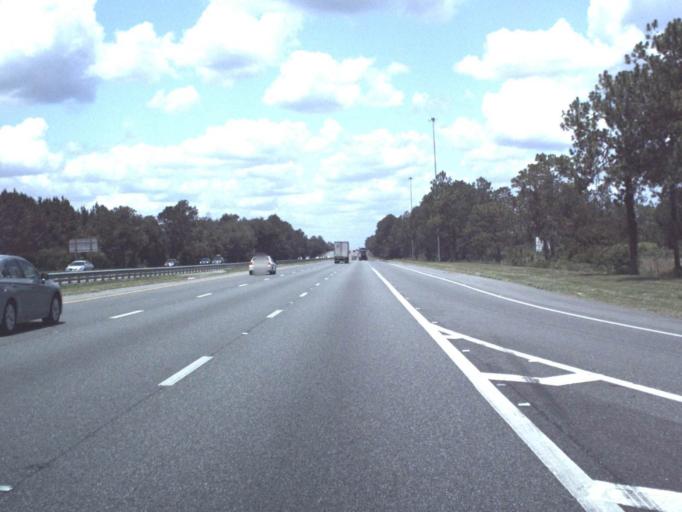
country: US
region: Florida
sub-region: Hamilton County
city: Jasper
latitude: 30.4506
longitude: -82.9358
